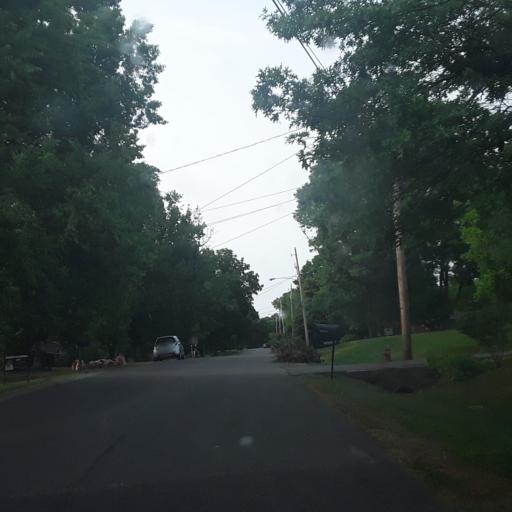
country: US
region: Tennessee
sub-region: Davidson County
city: Oak Hill
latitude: 36.0678
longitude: -86.7524
